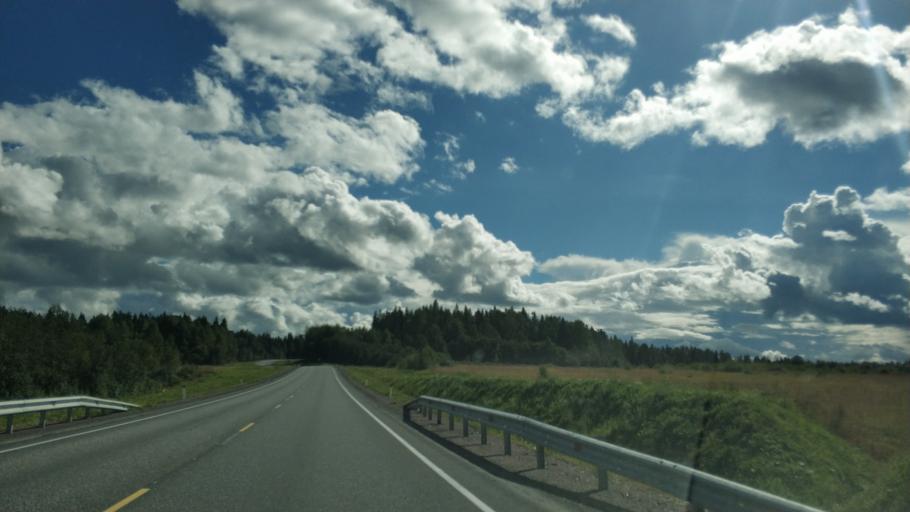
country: RU
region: Republic of Karelia
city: Ruskeala
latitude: 61.8731
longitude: 30.6491
